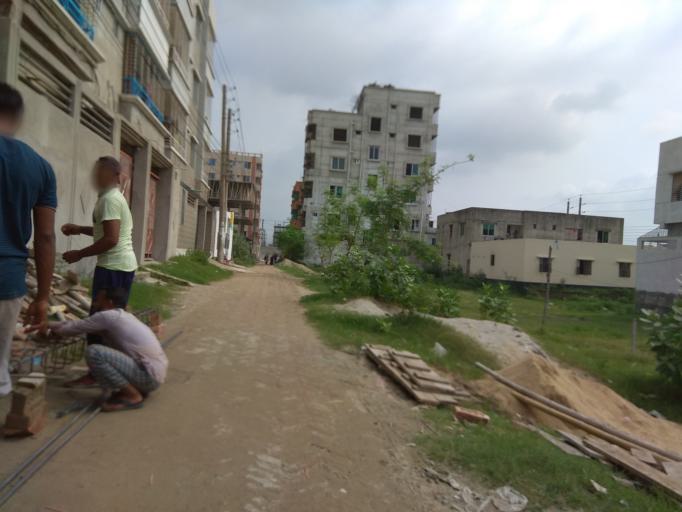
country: BD
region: Dhaka
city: Tungi
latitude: 23.8312
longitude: 90.3513
